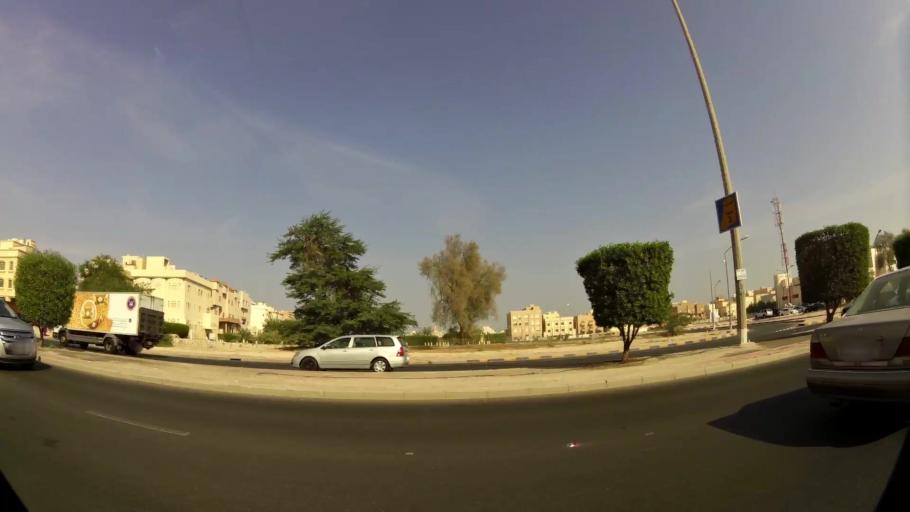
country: KW
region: Al Ahmadi
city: Ar Riqqah
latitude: 29.1644
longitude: 48.1017
